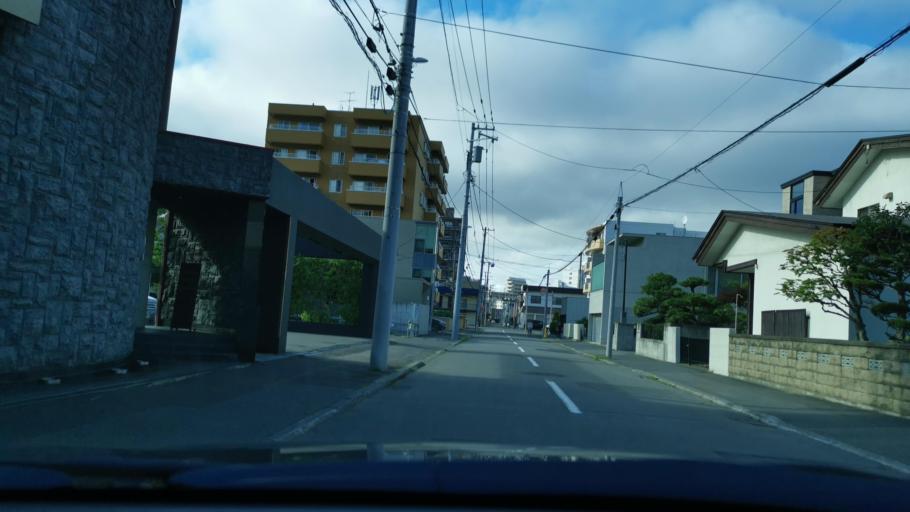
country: JP
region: Hokkaido
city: Sapporo
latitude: 43.0580
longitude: 141.3124
